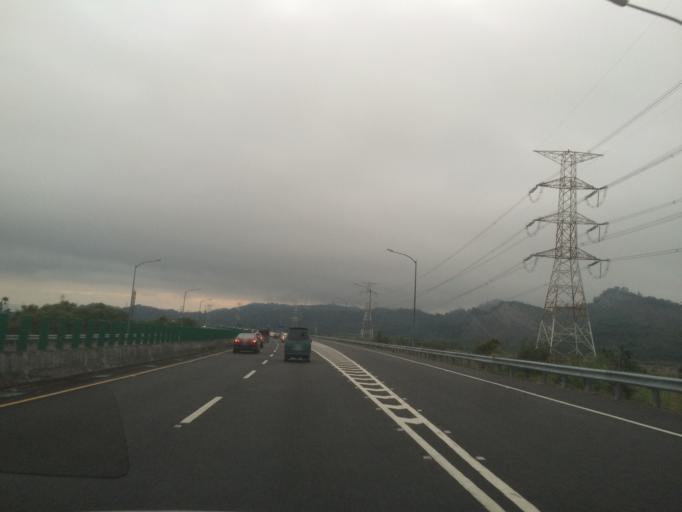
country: TW
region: Taiwan
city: Zhongxing New Village
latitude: 24.0015
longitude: 120.7383
